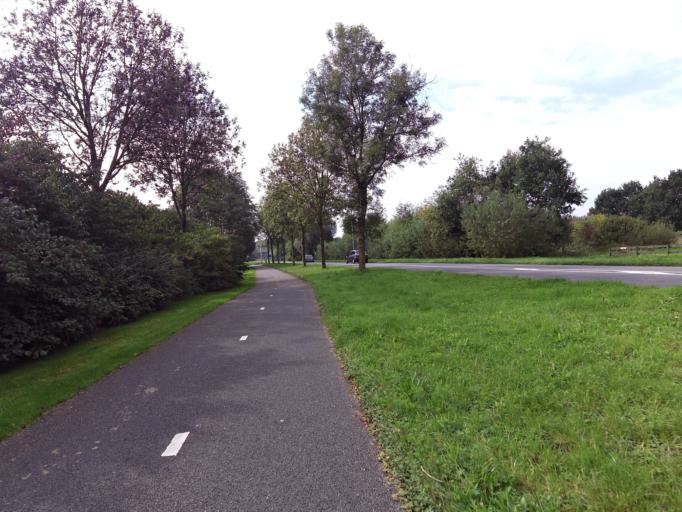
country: NL
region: Gelderland
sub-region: Gemeente Duiven
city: Duiven
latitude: 51.9536
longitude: 6.0048
